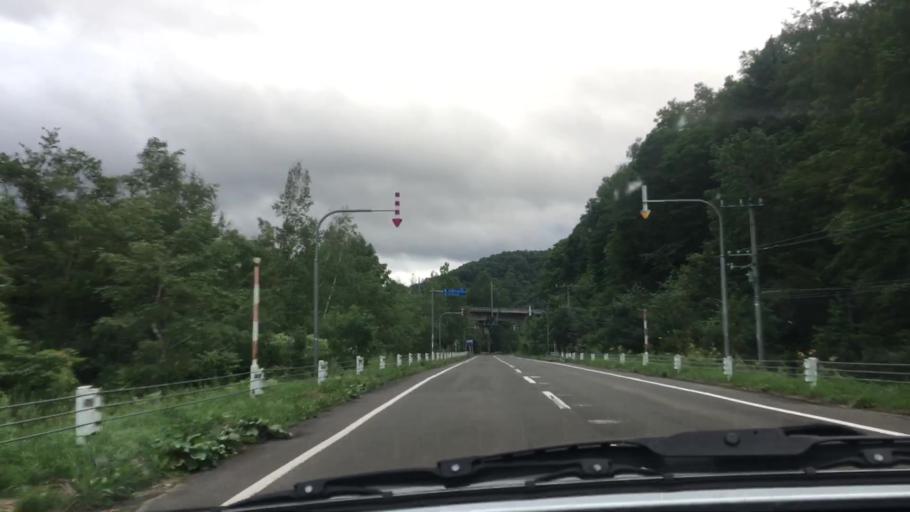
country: JP
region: Hokkaido
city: Shimo-furano
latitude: 43.0645
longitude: 142.5317
